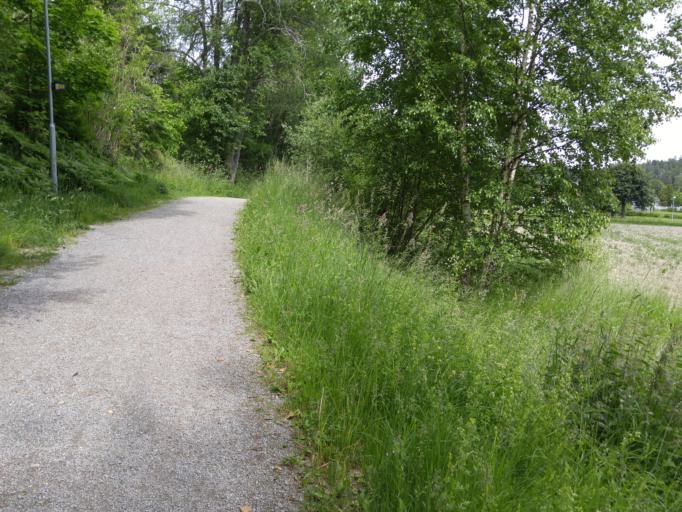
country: SE
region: Stockholm
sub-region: Sigtuna Kommun
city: Sigtuna
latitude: 59.6188
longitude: 17.7053
